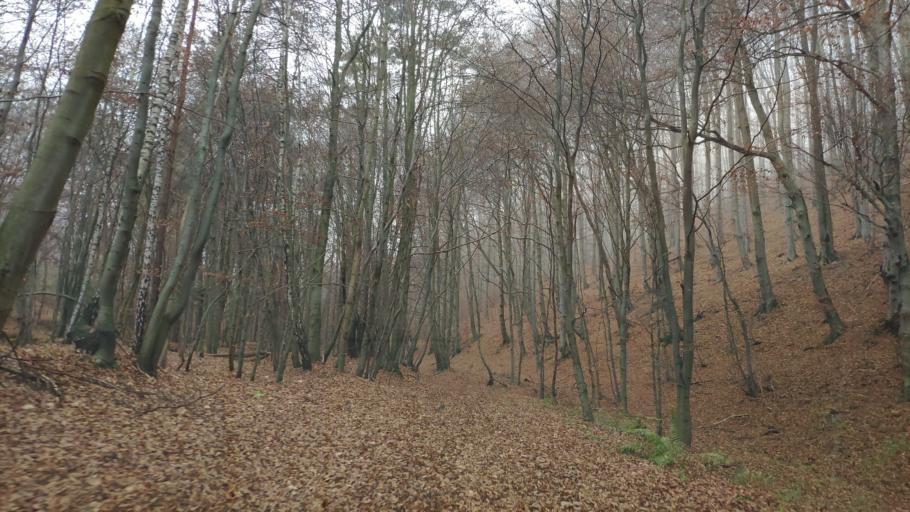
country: SK
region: Presovsky
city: Sabinov
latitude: 49.1499
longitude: 21.2093
